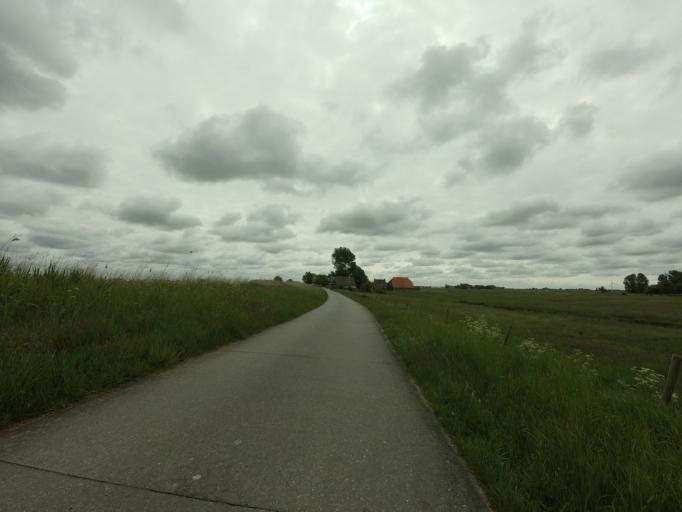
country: NL
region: Friesland
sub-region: Sudwest Fryslan
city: Workum
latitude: 53.0025
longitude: 5.4628
